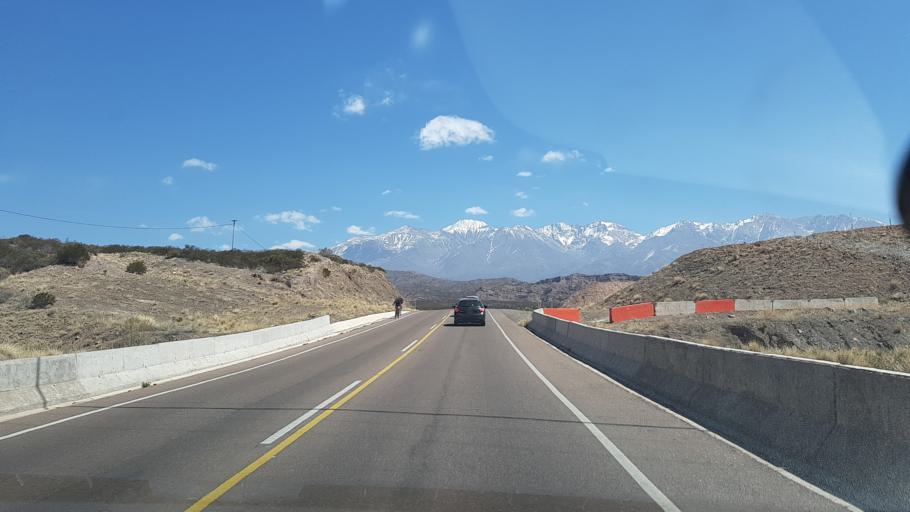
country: AR
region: Mendoza
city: Lujan de Cuyo
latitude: -32.9924
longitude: -69.1601
